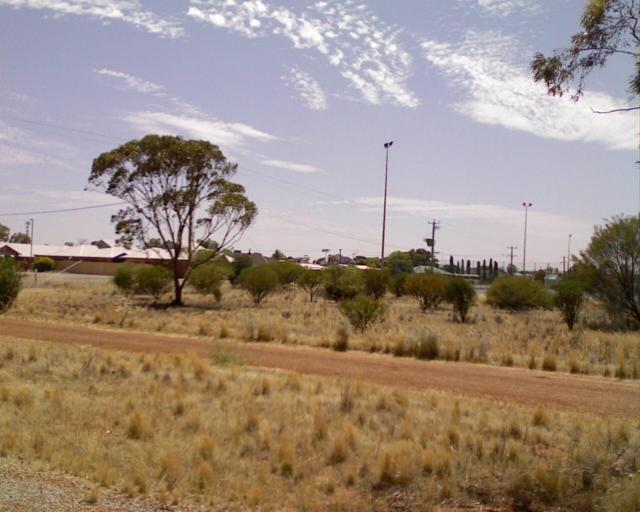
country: AU
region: Western Australia
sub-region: Merredin
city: Merredin
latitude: -30.9195
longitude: 118.2023
